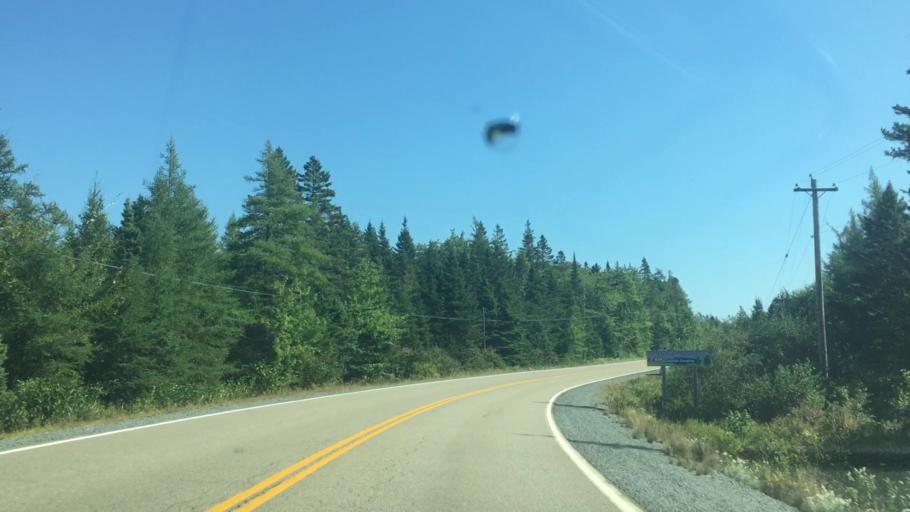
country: CA
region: Nova Scotia
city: Antigonish
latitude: 45.1446
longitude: -61.9961
